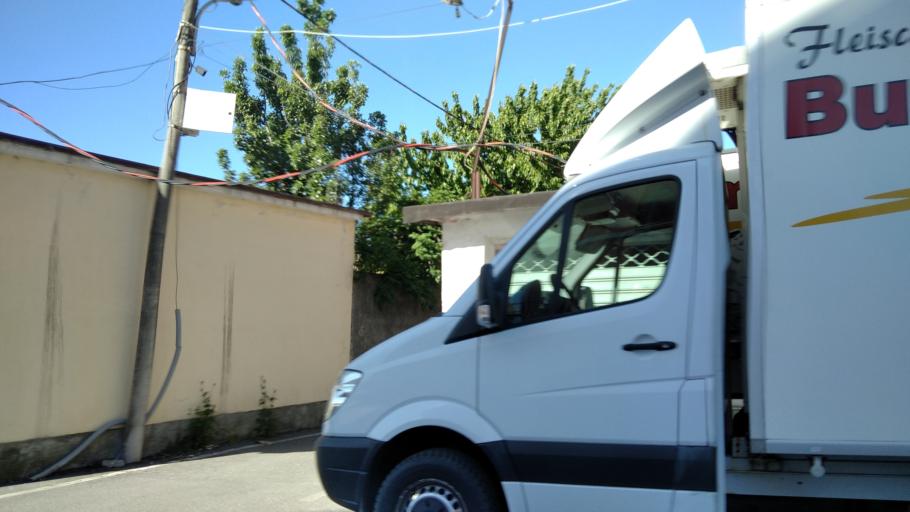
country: AL
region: Shkoder
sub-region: Rrethi i Shkodres
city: Shkoder
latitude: 42.0693
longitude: 19.5058
